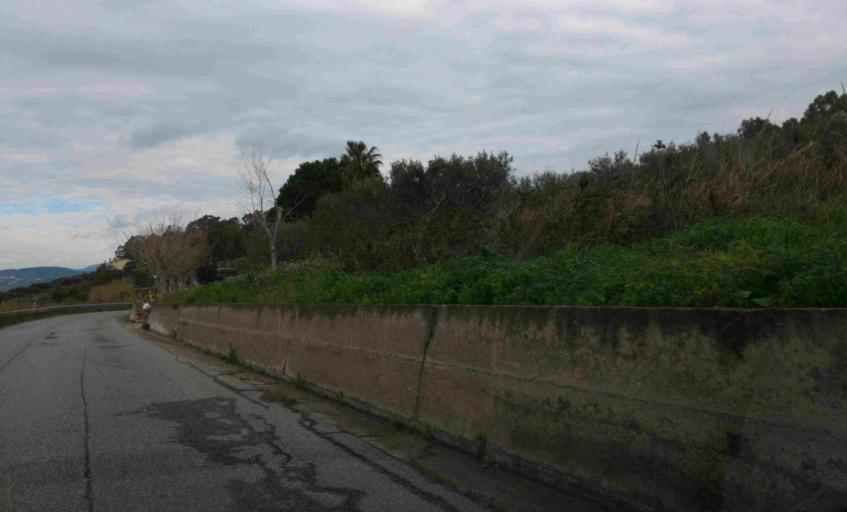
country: IT
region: Calabria
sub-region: Provincia di Catanzaro
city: Sellia Marina
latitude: 38.8866
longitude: 16.7107
